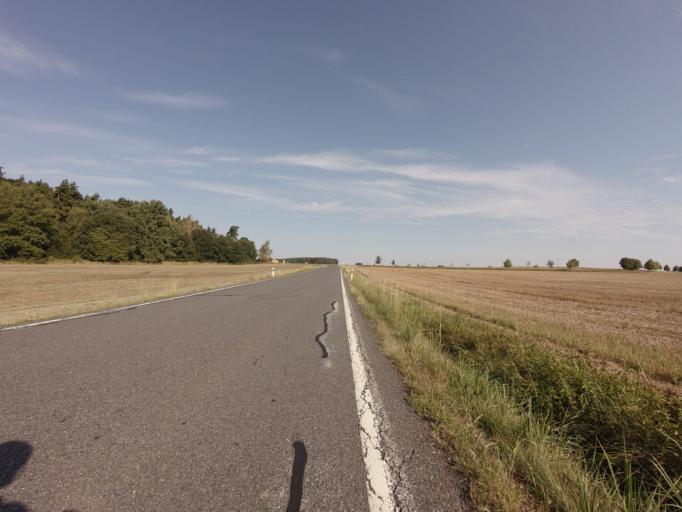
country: CZ
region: Jihocesky
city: Bernartice
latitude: 49.3172
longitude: 14.3701
